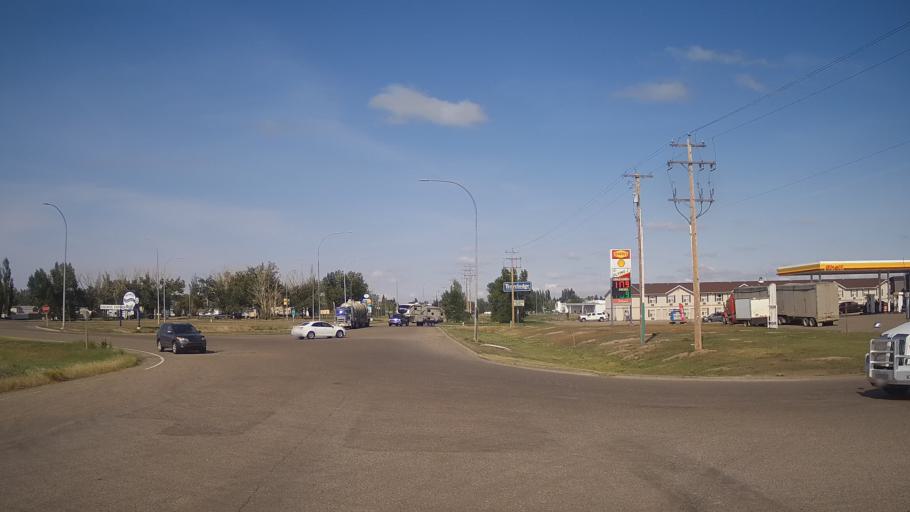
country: CA
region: Alberta
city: Brooks
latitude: 50.5722
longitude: -111.8667
